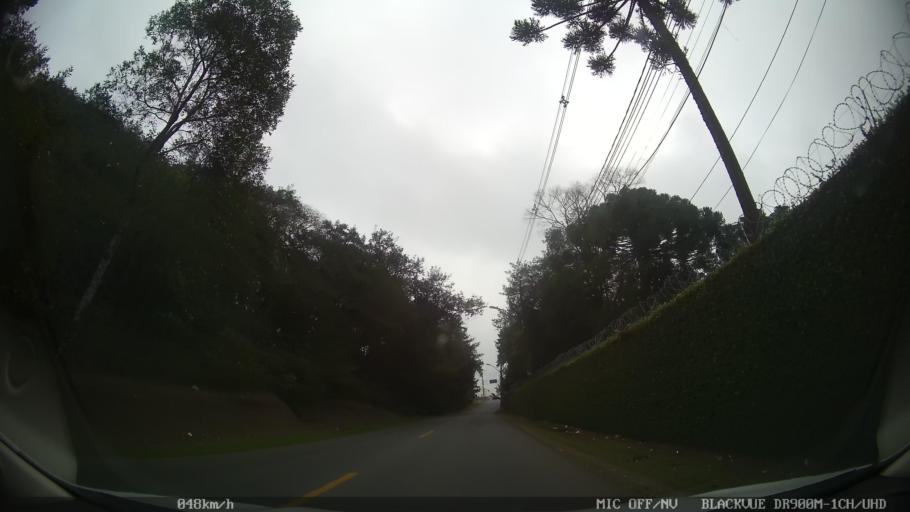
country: BR
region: Parana
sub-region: Almirante Tamandare
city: Almirante Tamandare
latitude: -25.3870
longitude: -49.3216
